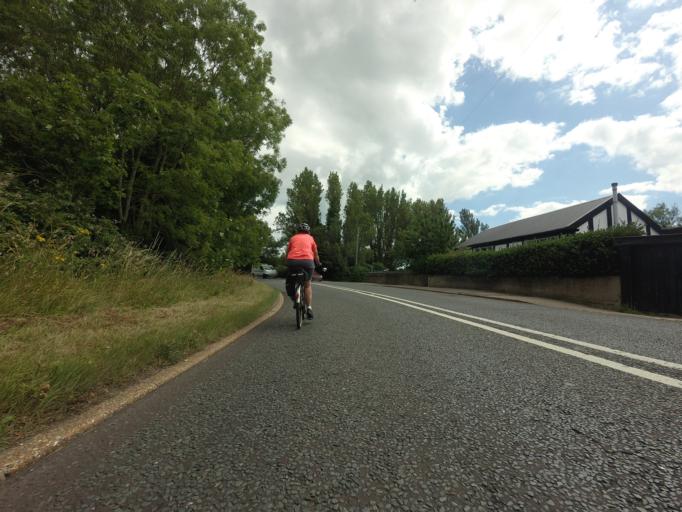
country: GB
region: England
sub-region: East Sussex
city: Pevensey
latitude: 50.8189
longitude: 0.3398
